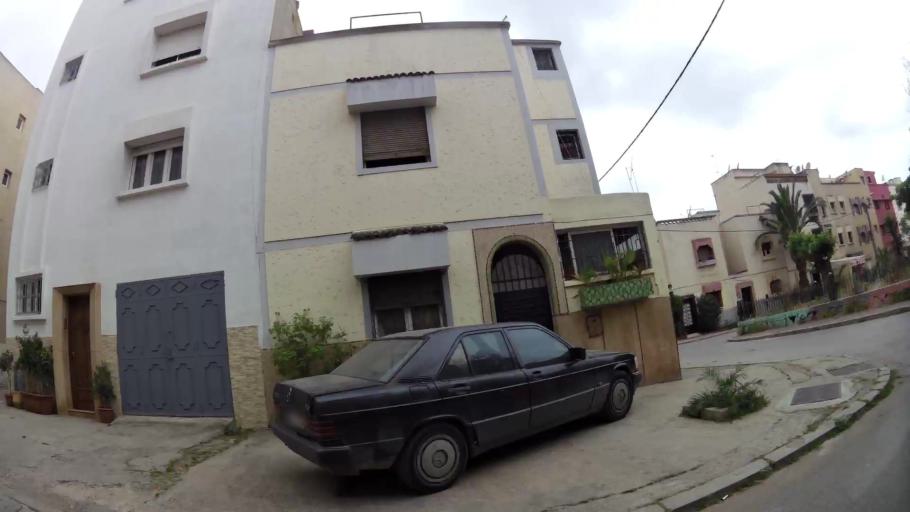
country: MA
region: Rabat-Sale-Zemmour-Zaer
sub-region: Rabat
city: Rabat
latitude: 33.9778
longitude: -6.8216
